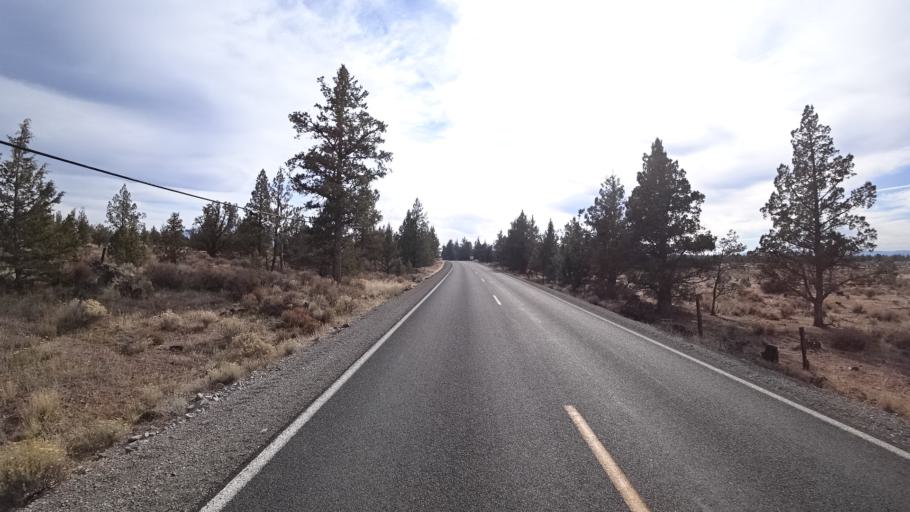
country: US
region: California
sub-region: Siskiyou County
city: Montague
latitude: 41.6556
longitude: -122.3995
